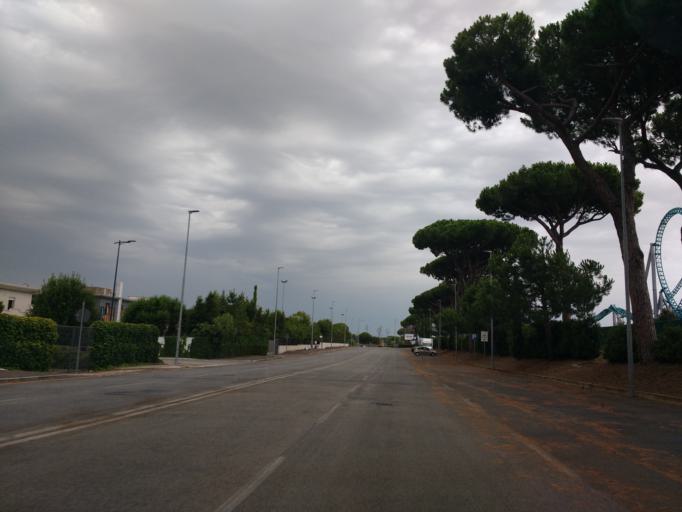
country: IT
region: Latium
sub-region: Citta metropolitana di Roma Capitale
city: Monte Migliore-La Selvotta
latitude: 41.7149
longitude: 12.4491
